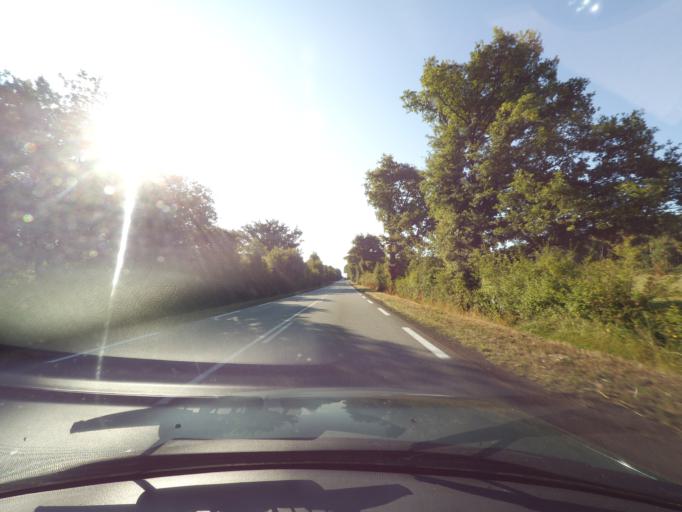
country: FR
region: Poitou-Charentes
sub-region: Departement des Deux-Sevres
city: Chiche
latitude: 46.8142
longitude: -0.3956
